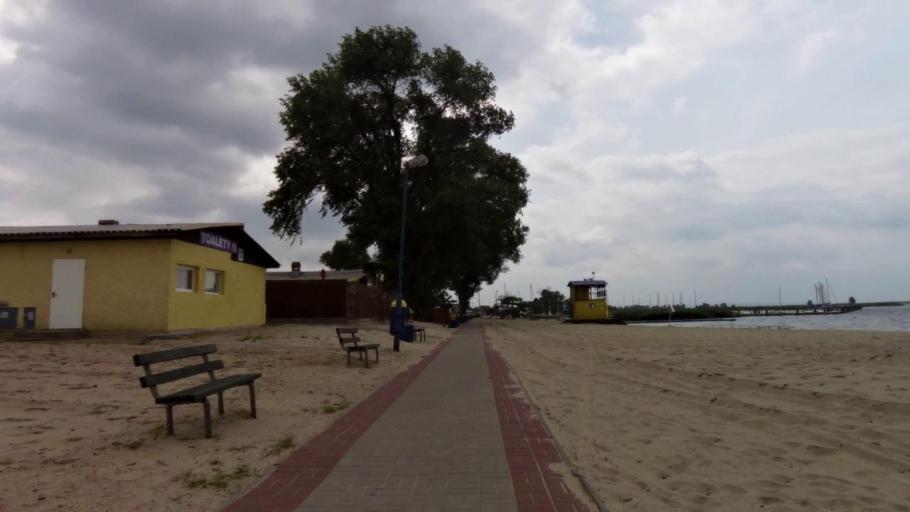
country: PL
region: West Pomeranian Voivodeship
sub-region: Powiat policki
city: Police
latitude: 53.5065
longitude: 14.7010
